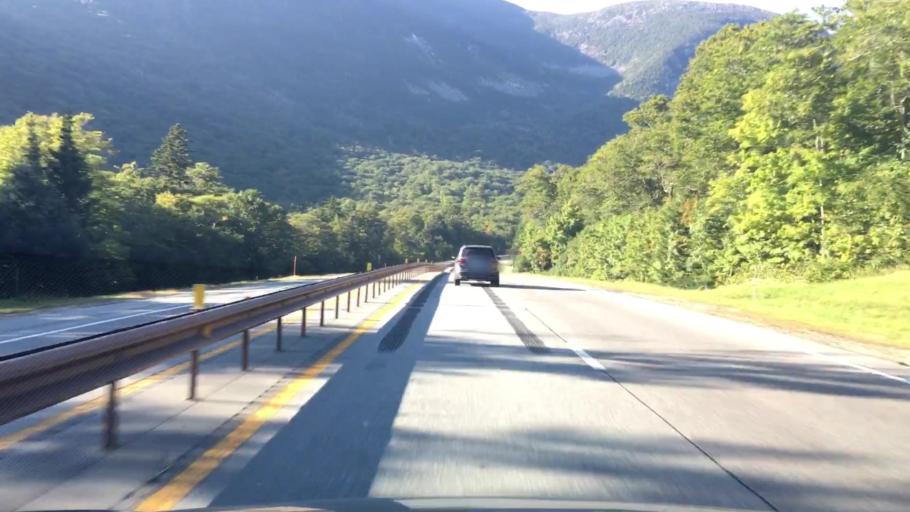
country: US
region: New Hampshire
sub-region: Grafton County
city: Deerfield
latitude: 44.1360
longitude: -71.6826
